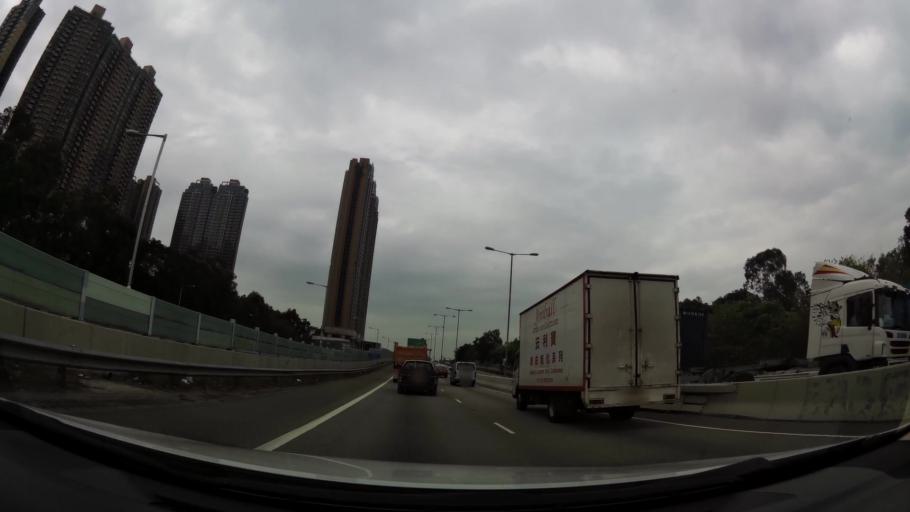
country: HK
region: Yuen Long
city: Yuen Long Kau Hui
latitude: 22.4421
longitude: 114.0394
